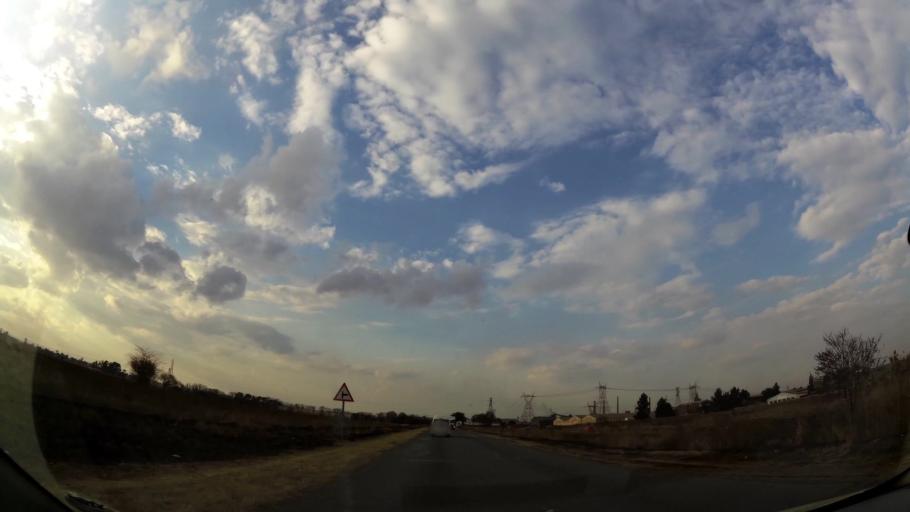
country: ZA
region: Gauteng
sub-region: Sedibeng District Municipality
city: Vanderbijlpark
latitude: -26.6657
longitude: 27.7963
